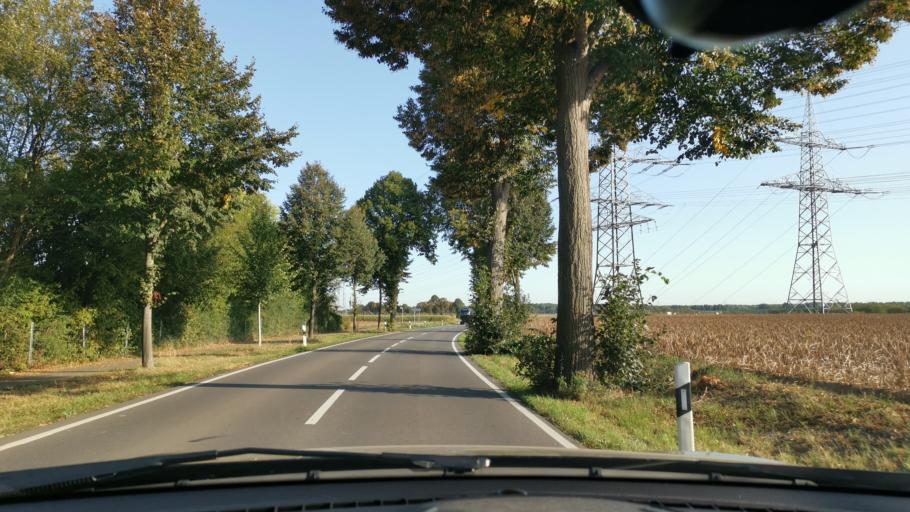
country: DE
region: North Rhine-Westphalia
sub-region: Regierungsbezirk Dusseldorf
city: Rommerskirchen
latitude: 51.0644
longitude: 6.7201
